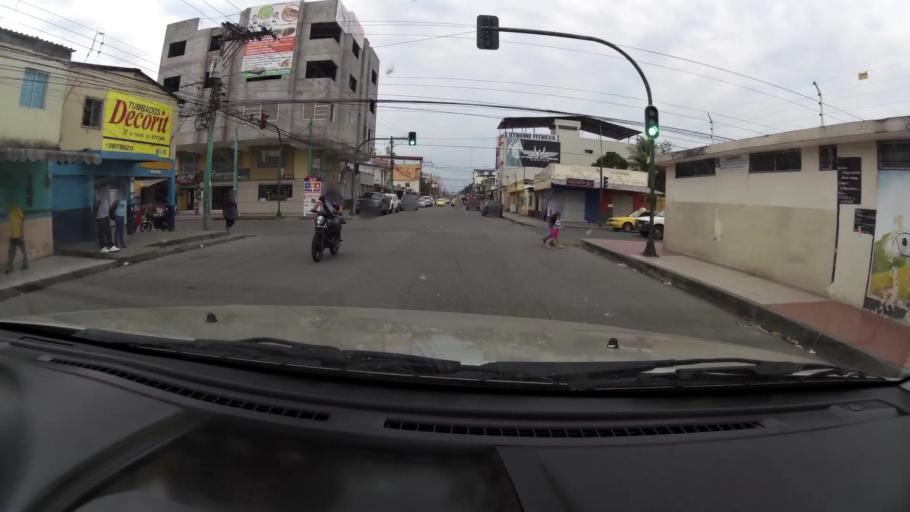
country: EC
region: El Oro
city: Machala
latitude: -3.2604
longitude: -79.9487
